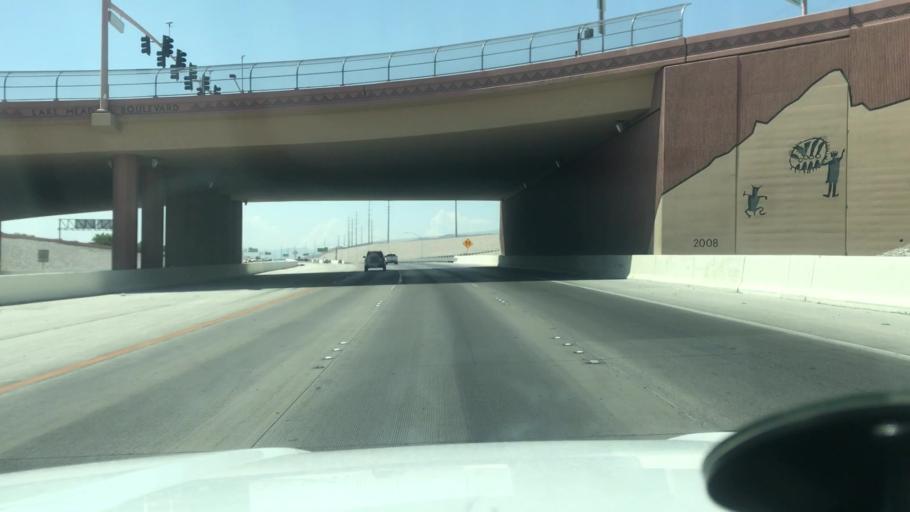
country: US
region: Nevada
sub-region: Clark County
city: Summerlin South
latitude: 36.2063
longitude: -115.3406
